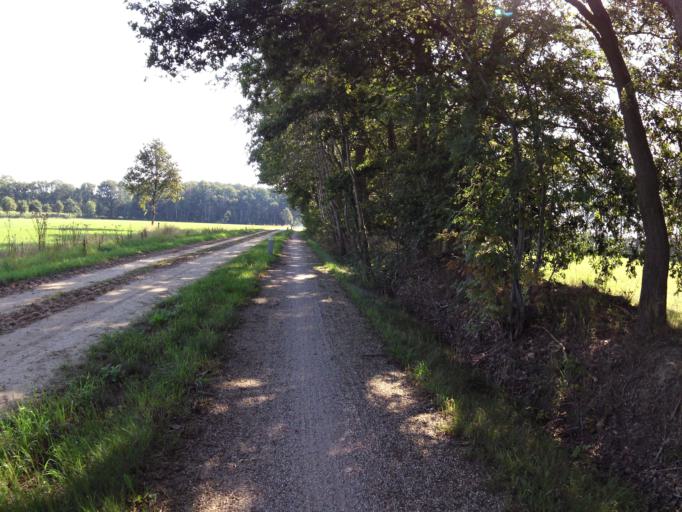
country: NL
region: Gelderland
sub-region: Gemeente Winterswijk
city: Winterswijk
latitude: 51.9709
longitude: 6.7621
